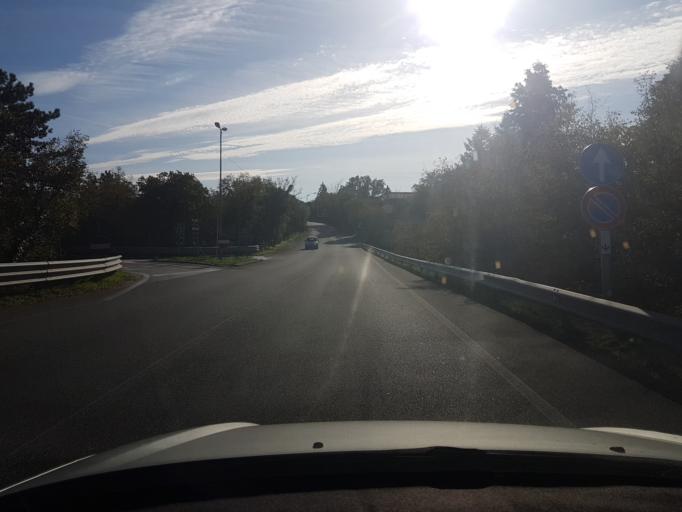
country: IT
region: Friuli Venezia Giulia
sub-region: Provincia di Trieste
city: Prosecco-Contovello
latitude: 45.7180
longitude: 13.7282
